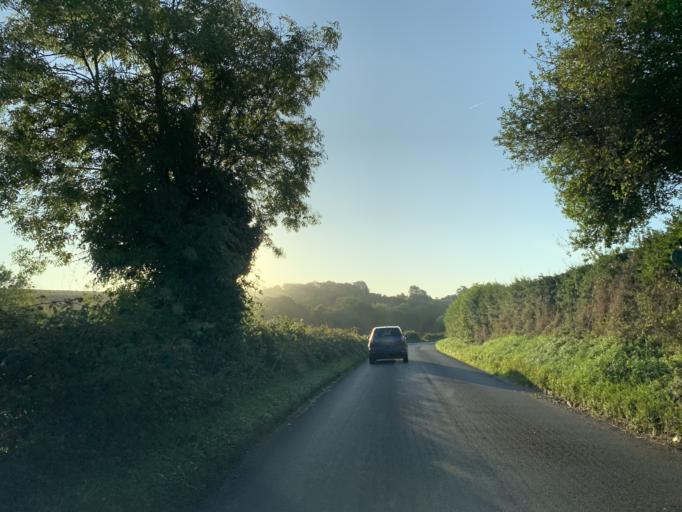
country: GB
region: England
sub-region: Wiltshire
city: Woodford
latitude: 51.1190
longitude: -1.8241
